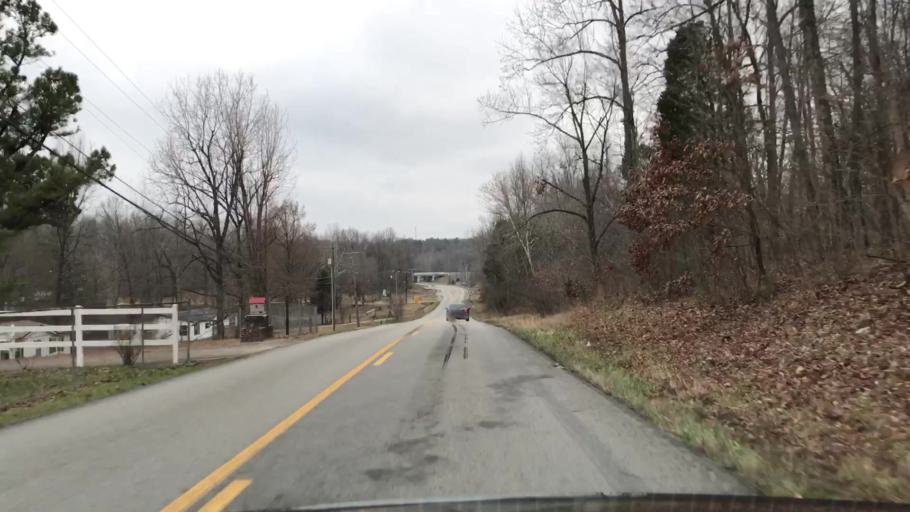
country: US
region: Kentucky
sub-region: Muhlenberg County
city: Morehead
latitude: 37.2472
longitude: -87.1957
